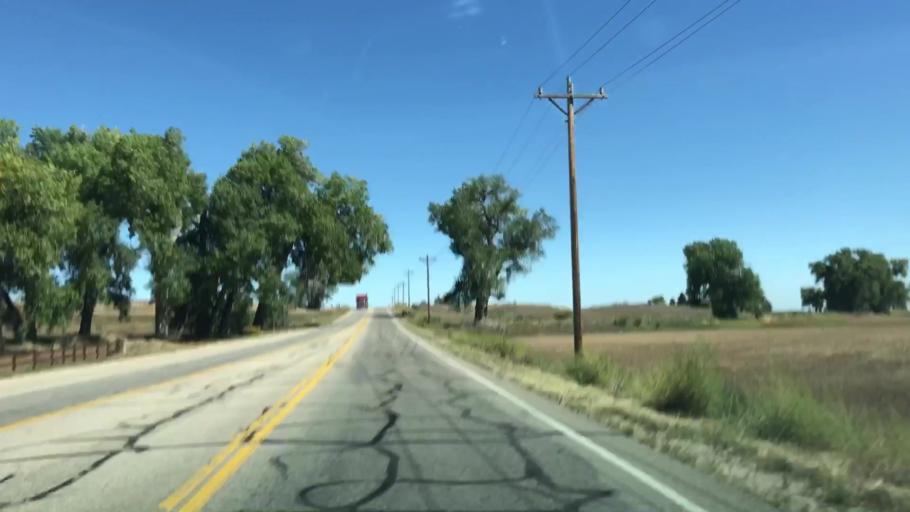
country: US
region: Colorado
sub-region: Weld County
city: Windsor
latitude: 40.5228
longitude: -104.9521
